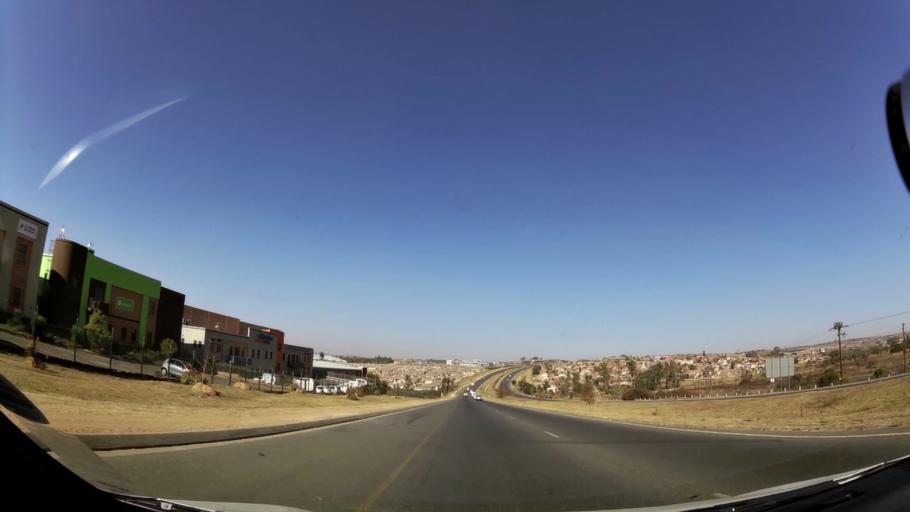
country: ZA
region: Gauteng
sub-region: West Rand District Municipality
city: Muldersdriseloop
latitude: -26.0076
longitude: 27.9334
